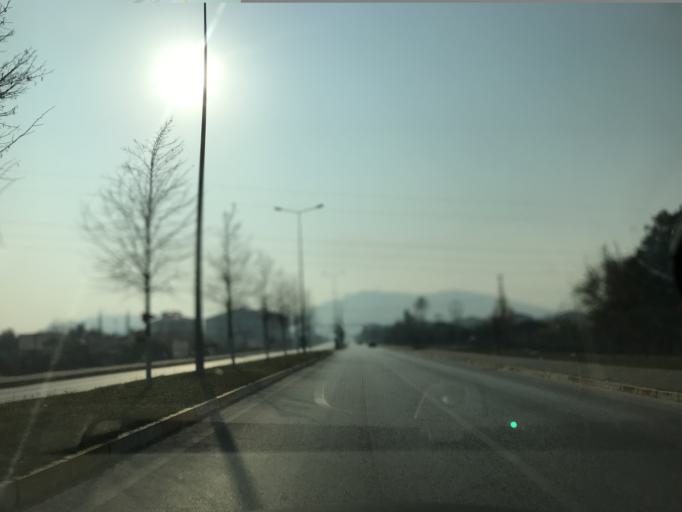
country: TR
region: Duzce
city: Cumayeri
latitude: 40.8630
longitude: 30.9532
